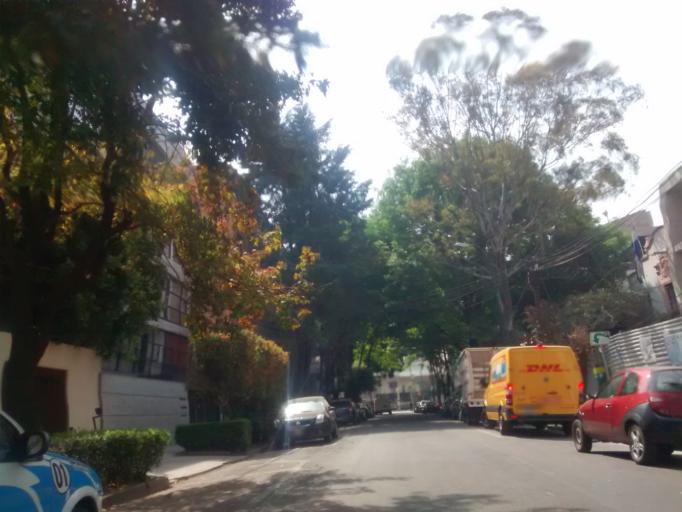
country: MX
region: Mexico City
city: Miguel Hidalgo
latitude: 19.4326
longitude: -99.1918
